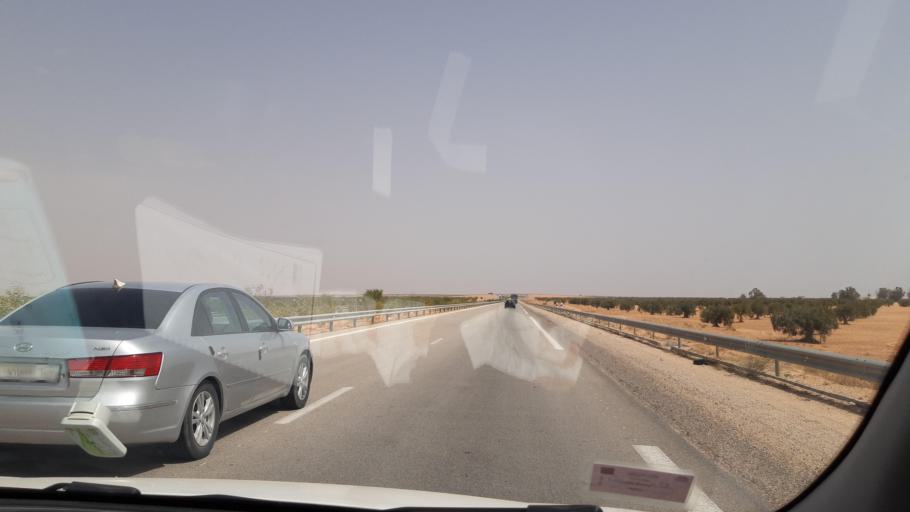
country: TN
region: Safaqis
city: Bi'r `Ali Bin Khalifah
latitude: 34.5299
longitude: 10.1081
